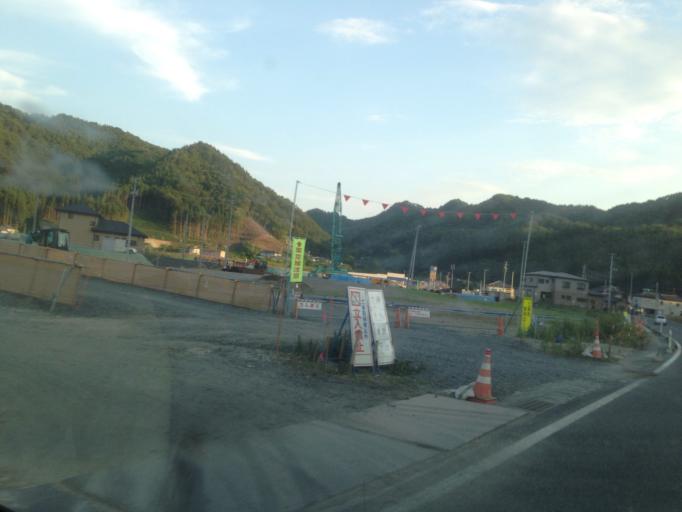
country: JP
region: Iwate
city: Otsuchi
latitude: 39.3248
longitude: 141.8855
